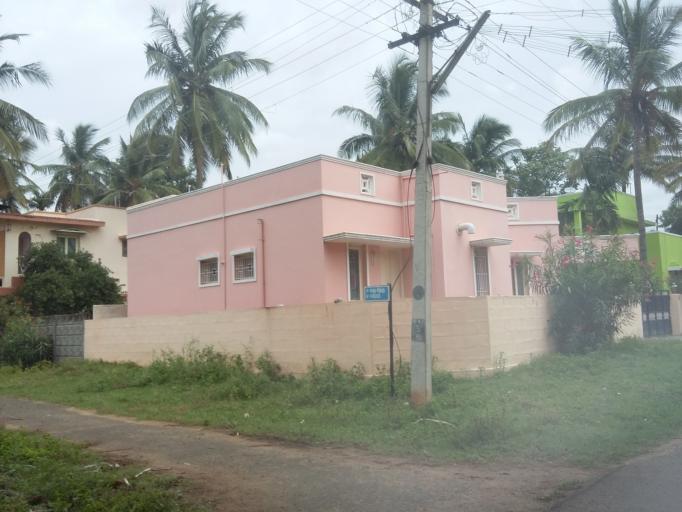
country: IN
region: Tamil Nadu
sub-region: Coimbatore
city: Perur
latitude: 11.0304
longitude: 76.8983
